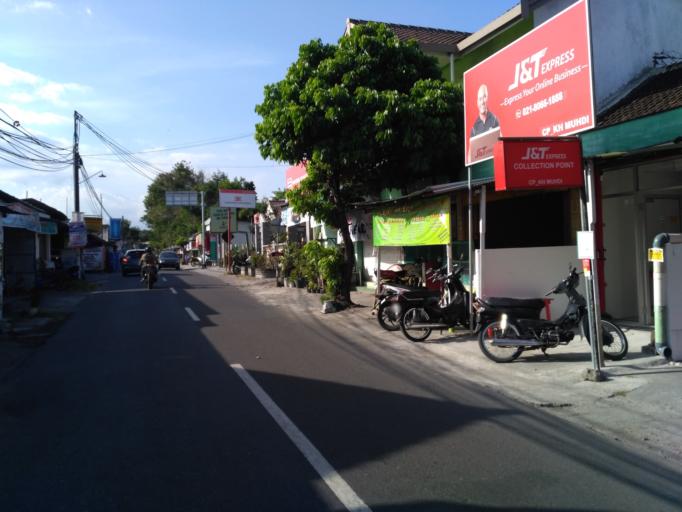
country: ID
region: Daerah Istimewa Yogyakarta
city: Depok
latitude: -7.7832
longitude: 110.4226
